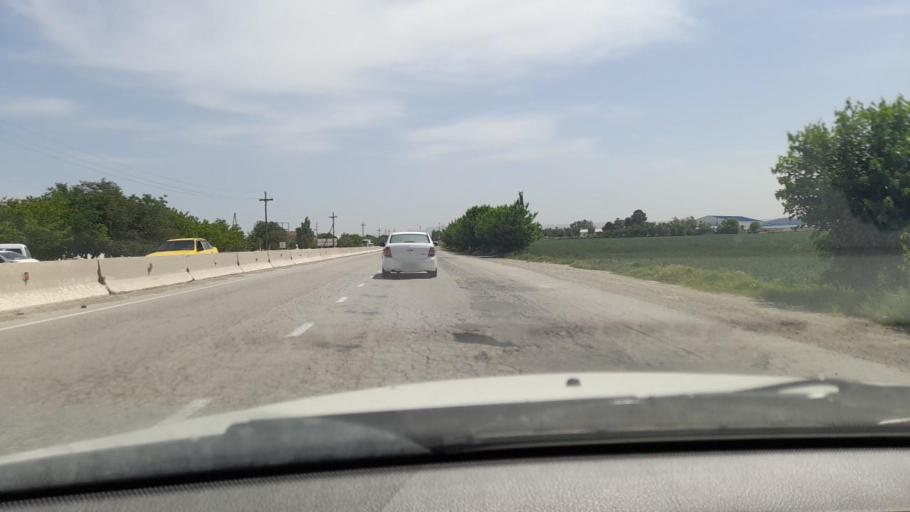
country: UZ
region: Navoiy
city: Karmana Shahri
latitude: 40.1354
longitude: 65.4042
